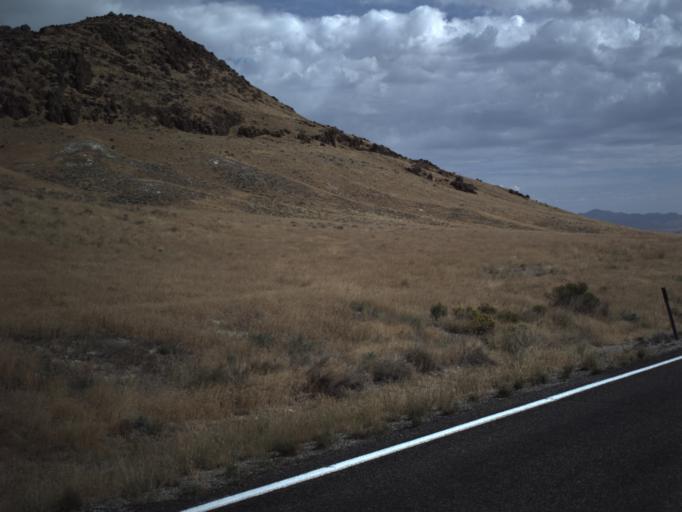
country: US
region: Utah
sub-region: Tooele County
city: Wendover
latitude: 41.3778
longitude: -114.0040
